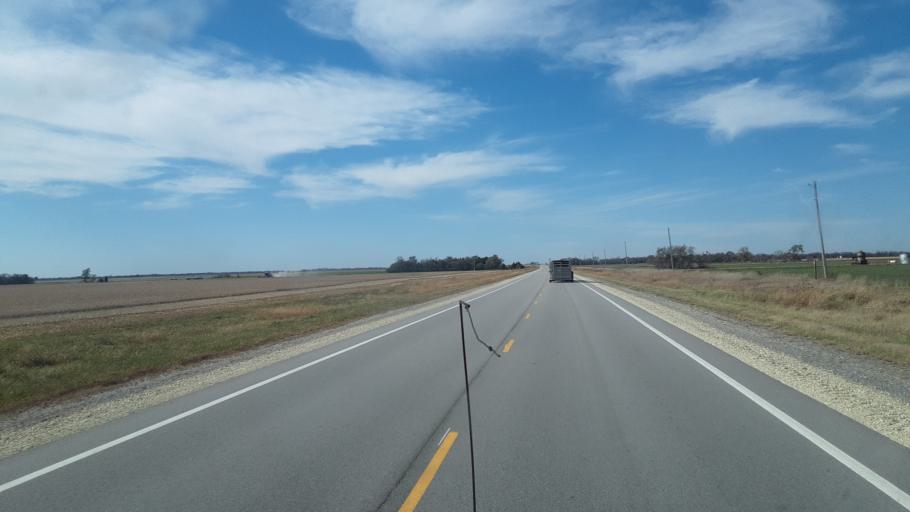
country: US
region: Kansas
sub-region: Marion County
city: Hillsboro
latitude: 38.3771
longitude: -97.3834
